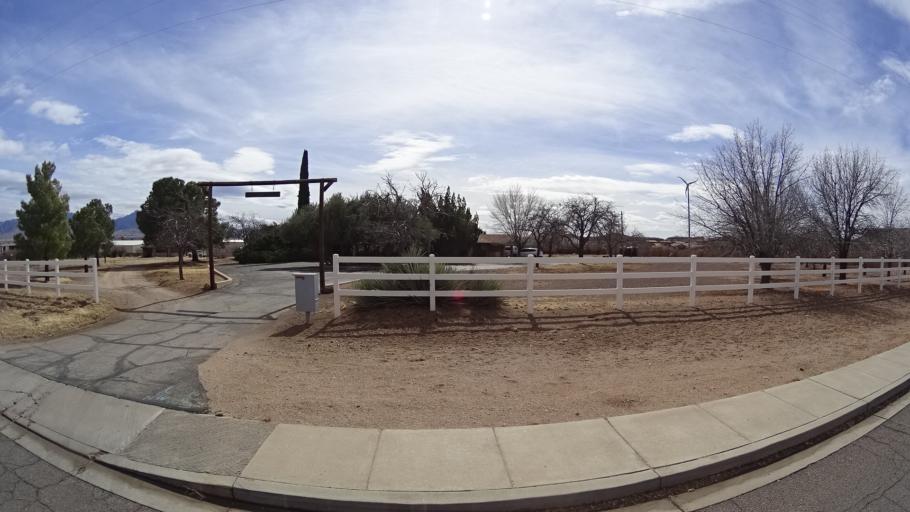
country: US
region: Arizona
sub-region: Mohave County
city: New Kingman-Butler
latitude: 35.2296
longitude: -114.0398
